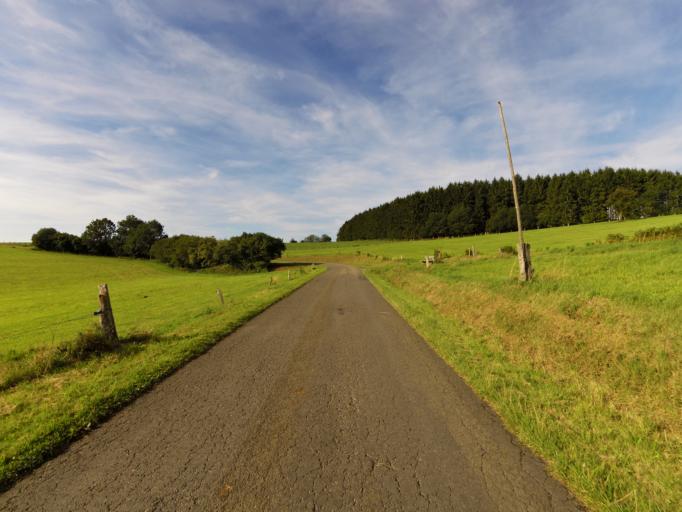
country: BE
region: Wallonia
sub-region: Province du Luxembourg
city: Erezee
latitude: 50.2545
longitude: 5.5530
